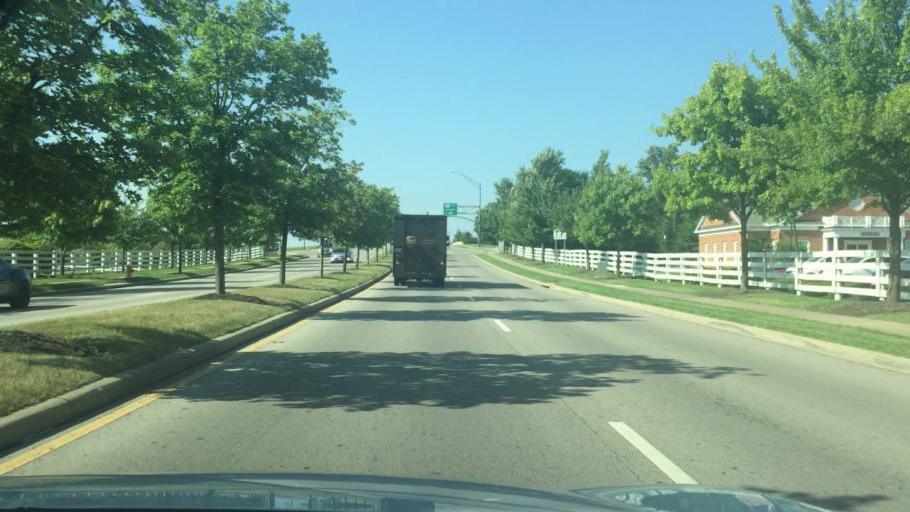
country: US
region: Ohio
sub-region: Franklin County
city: New Albany
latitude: 40.0890
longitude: -82.8232
